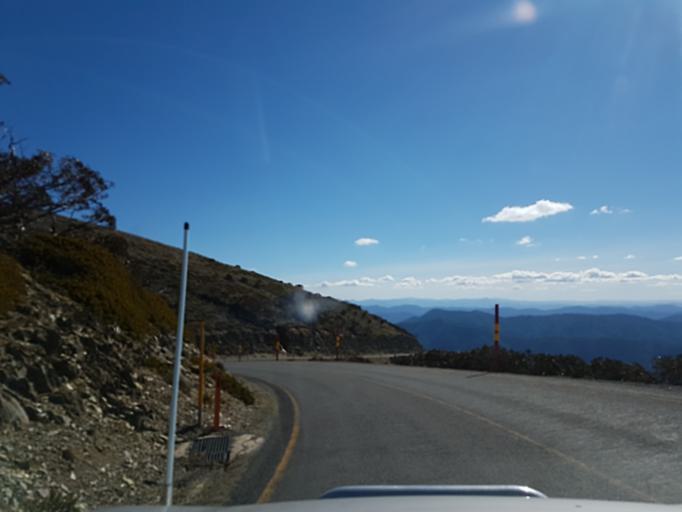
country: AU
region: Victoria
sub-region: Alpine
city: Mount Beauty
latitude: -36.9729
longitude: 147.1294
